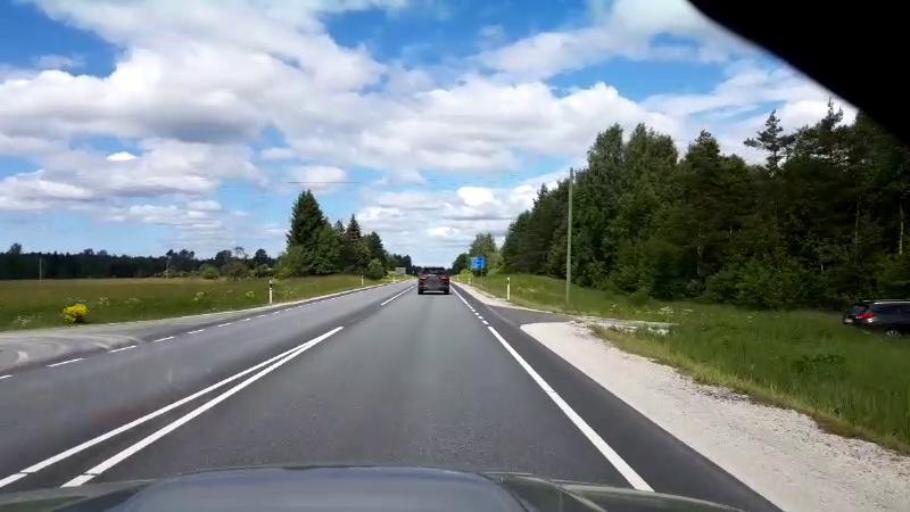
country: EE
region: Raplamaa
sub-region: Maerjamaa vald
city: Marjamaa
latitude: 59.0508
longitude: 24.4451
